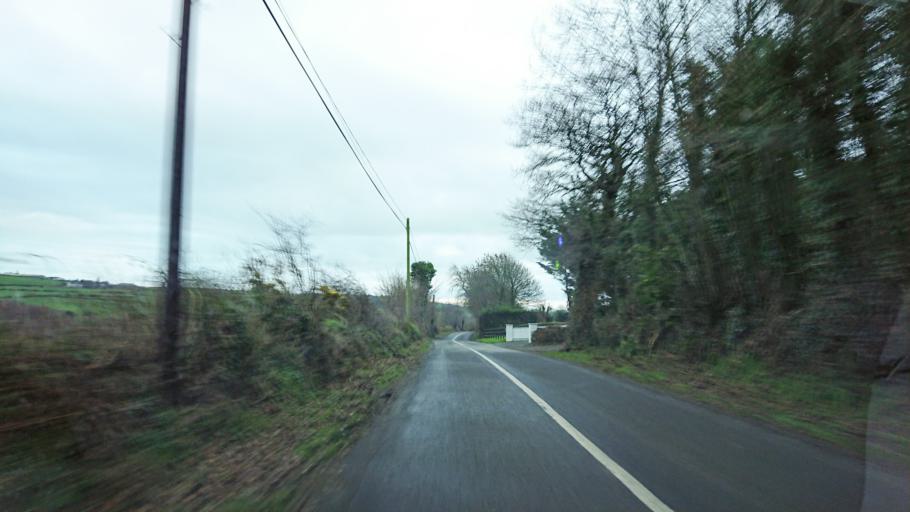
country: IE
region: Munster
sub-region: Waterford
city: Portlaw
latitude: 52.1664
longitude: -7.3899
